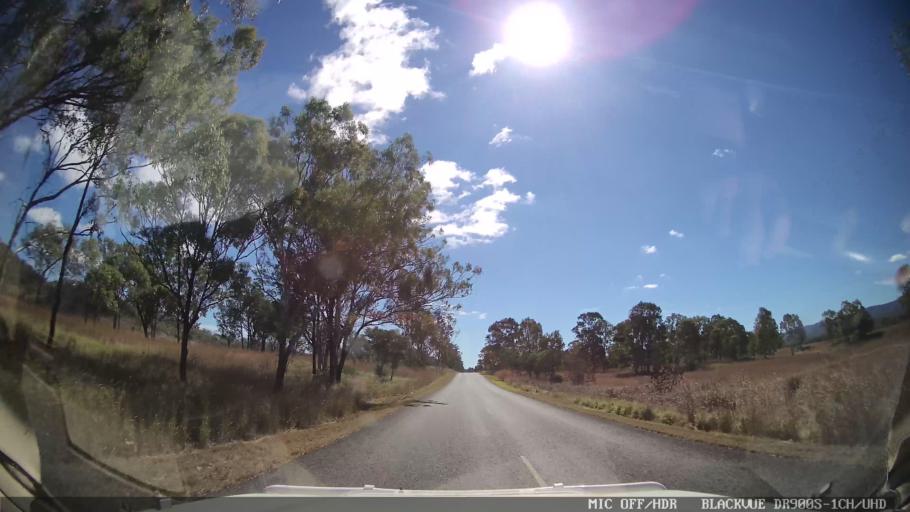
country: AU
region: Queensland
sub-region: Gladstone
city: Toolooa
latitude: -24.4461
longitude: 151.3430
